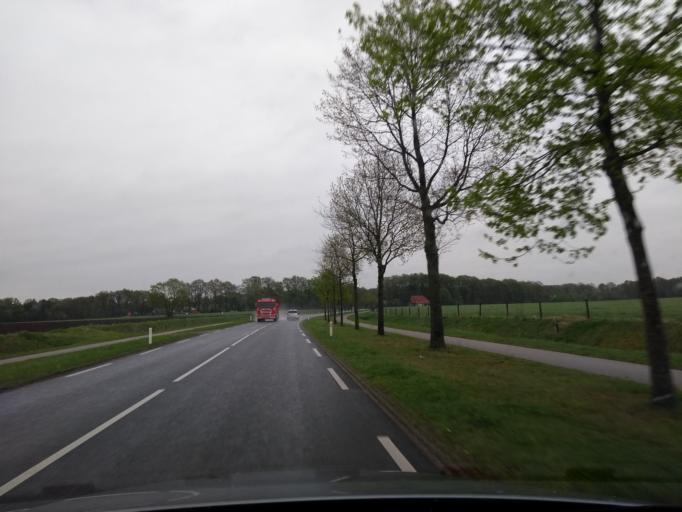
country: NL
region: Overijssel
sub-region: Gemeente Tubbergen
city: Tubbergen
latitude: 52.3987
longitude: 6.8521
